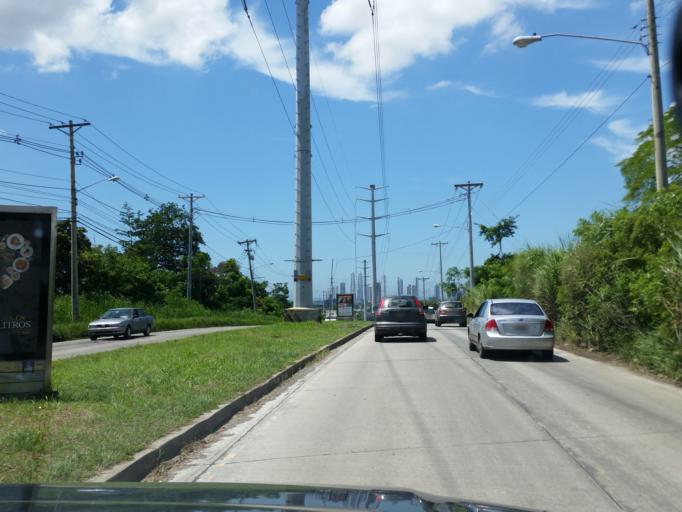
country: PA
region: Panama
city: San Miguelito
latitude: 9.0646
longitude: -79.4620
